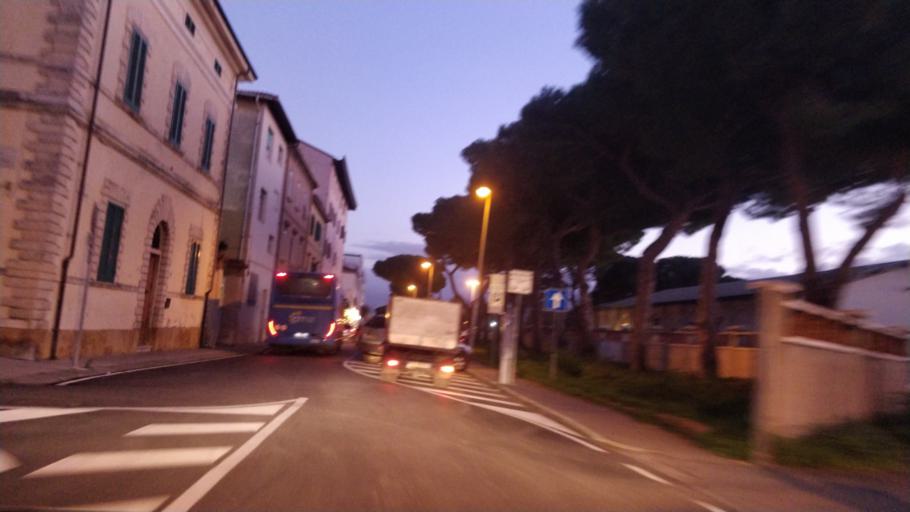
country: IT
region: Tuscany
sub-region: Provincia di Livorno
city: Cecina
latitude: 43.3117
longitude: 10.5143
